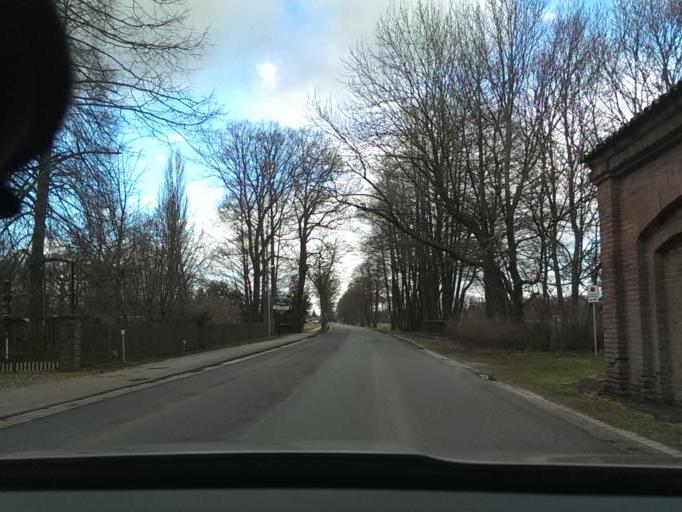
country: DE
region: Lower Saxony
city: Elze
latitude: 52.5744
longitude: 9.7193
